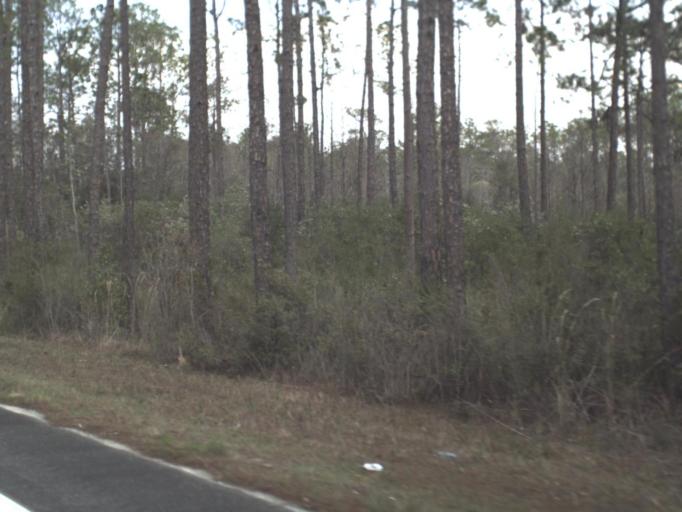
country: US
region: Florida
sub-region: Franklin County
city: Apalachicola
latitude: 29.9683
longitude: -84.9755
